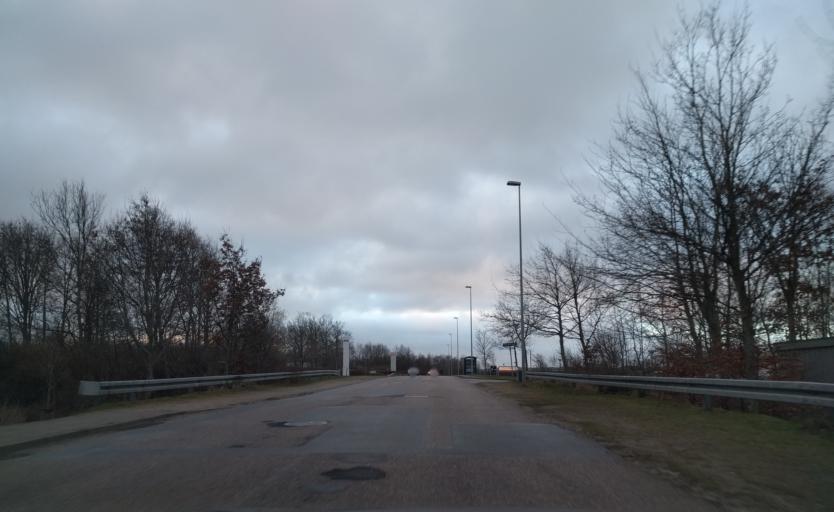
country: DK
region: North Denmark
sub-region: Alborg Kommune
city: Gistrup
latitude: 57.0141
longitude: 9.9842
